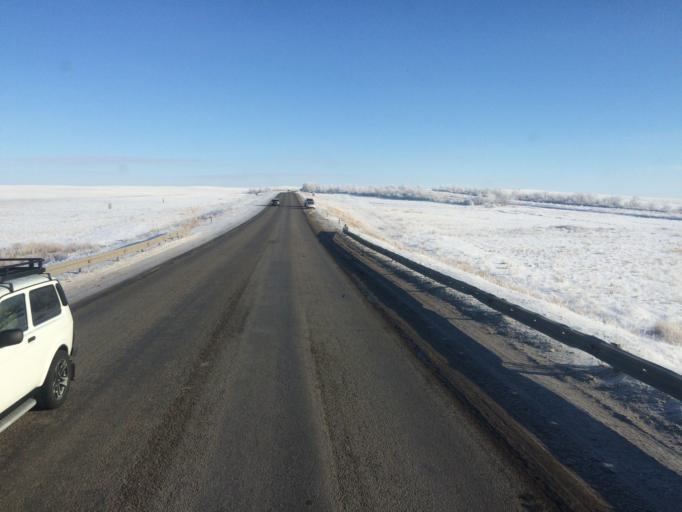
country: KZ
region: Aqtoebe
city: Aqtobe
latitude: 50.2830
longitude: 57.7617
